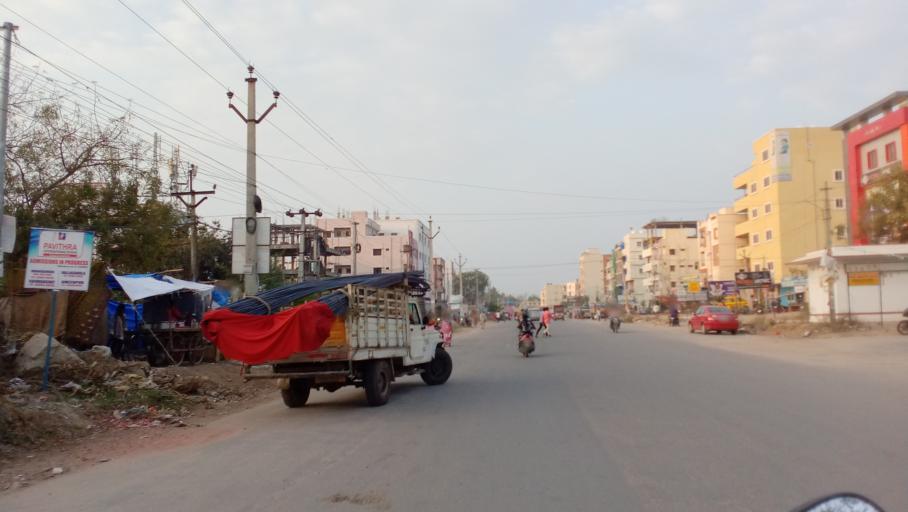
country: IN
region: Telangana
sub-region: Medak
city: Serilingampalle
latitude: 17.5055
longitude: 78.3182
